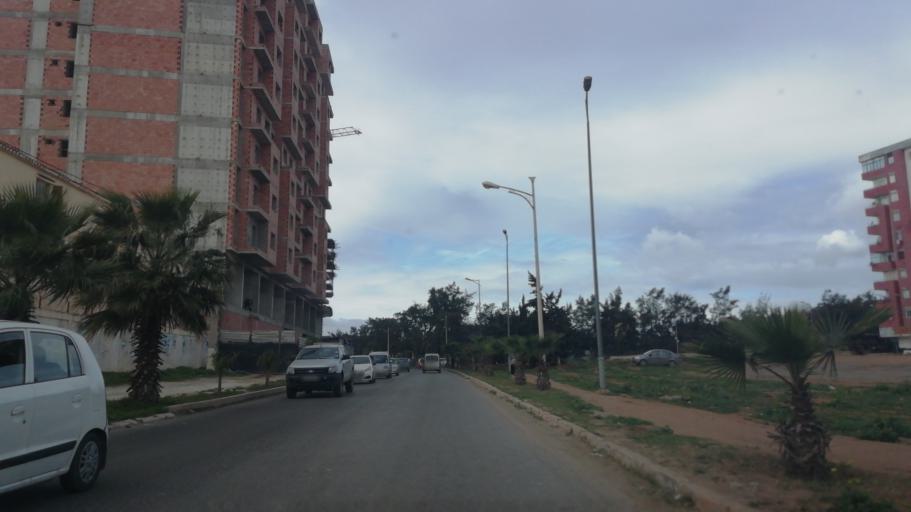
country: DZ
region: Oran
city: Bir el Djir
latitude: 35.7158
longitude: -0.5753
